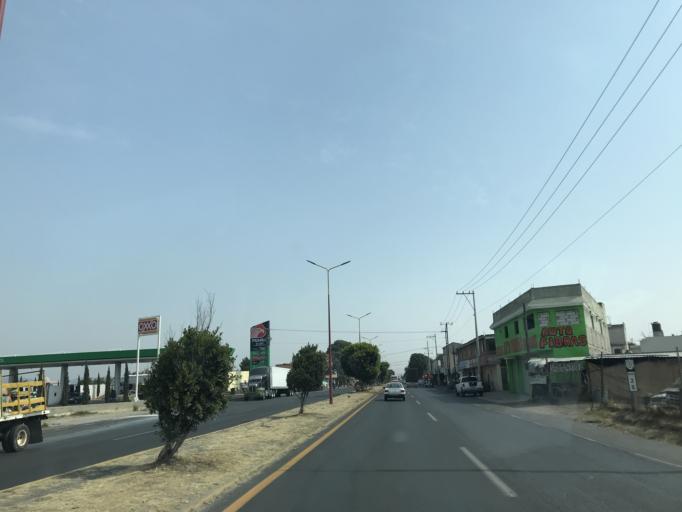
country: MX
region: Tlaxcala
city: La Magdalena Tlaltelulco
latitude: 19.2789
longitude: -98.1963
